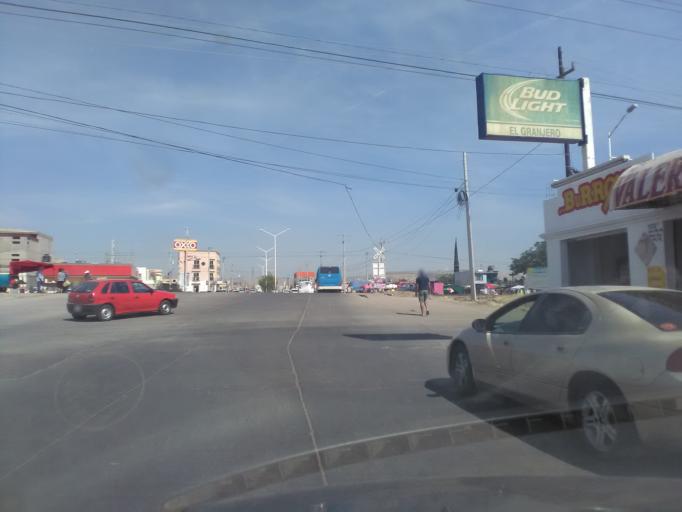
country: MX
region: Durango
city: Victoria de Durango
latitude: 24.0559
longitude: -104.6288
